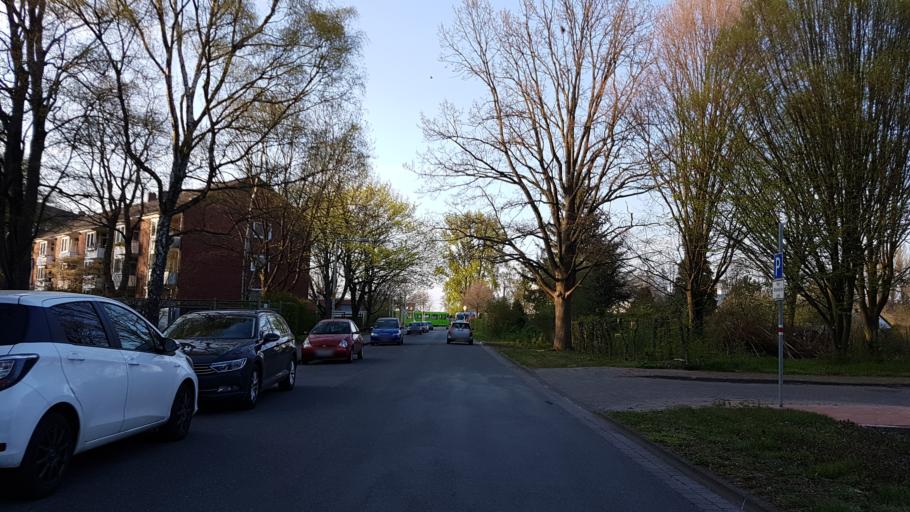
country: DE
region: Lower Saxony
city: Hannover
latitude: 52.3587
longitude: 9.6873
